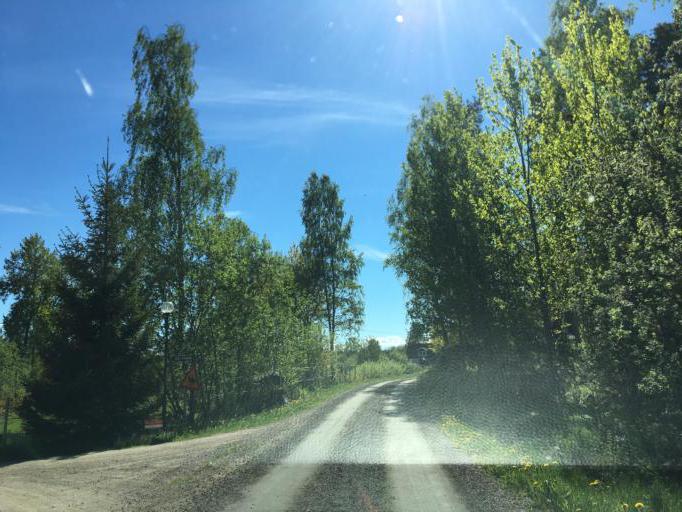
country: SE
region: Soedermanland
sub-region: Eskilstuna Kommun
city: Hallbybrunn
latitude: 59.3544
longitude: 16.3463
